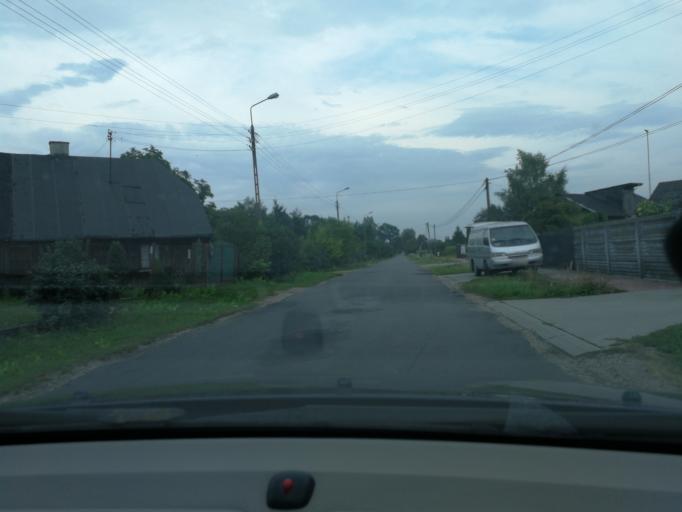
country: PL
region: Masovian Voivodeship
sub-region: Powiat grodziski
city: Grodzisk Mazowiecki
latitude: 52.1276
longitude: 20.6071
